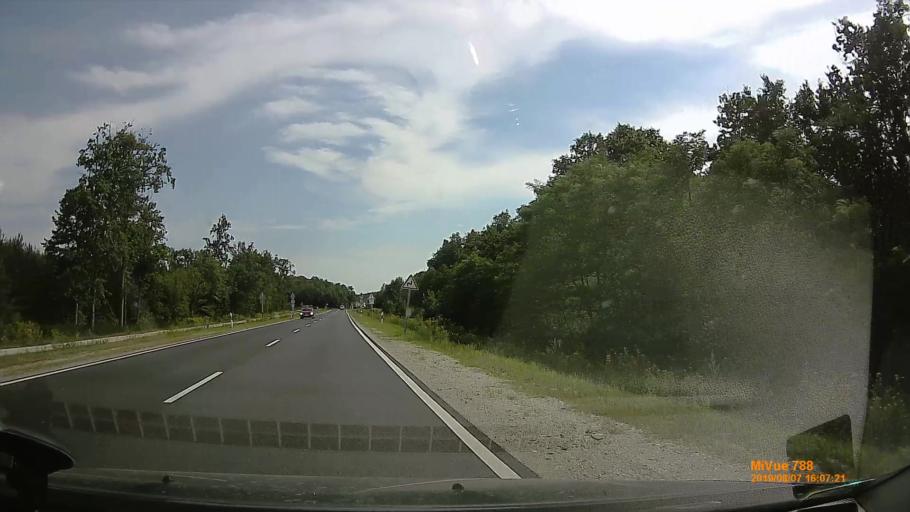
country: HU
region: Zala
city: Zalalovo
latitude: 46.9221
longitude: 16.5997
